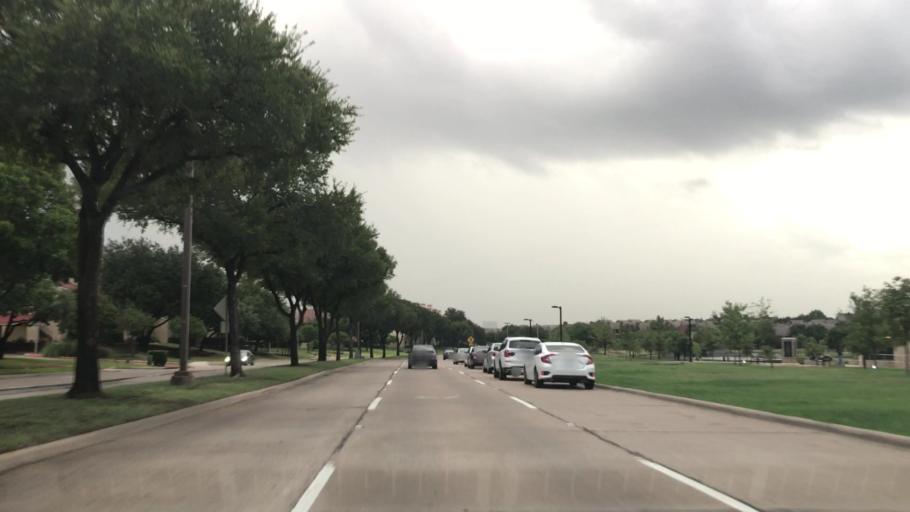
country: US
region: Texas
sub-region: Dallas County
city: Irving
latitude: 32.8822
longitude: -96.9695
